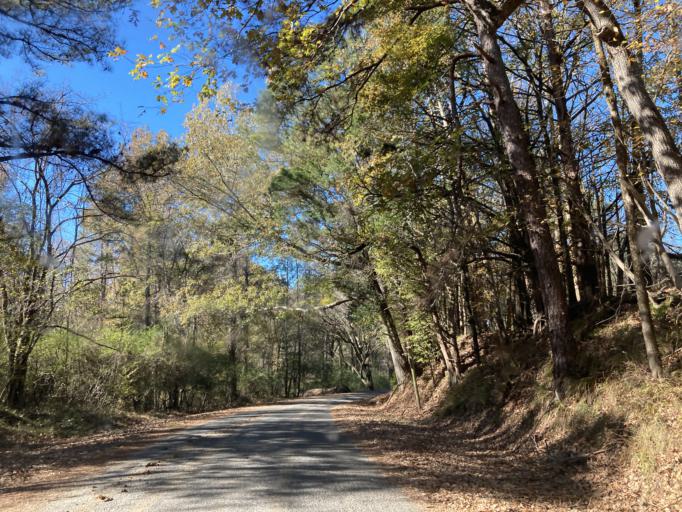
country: US
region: Mississippi
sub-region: Hinds County
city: Lynchburg
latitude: 32.5804
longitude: -90.5613
